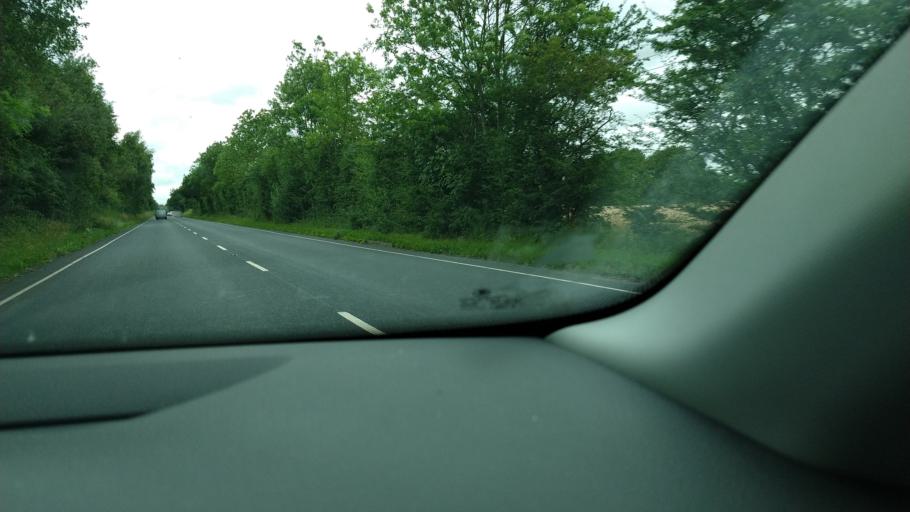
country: GB
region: England
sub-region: East Riding of Yorkshire
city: Barmby on the Marsh
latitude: 53.7194
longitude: -0.9725
